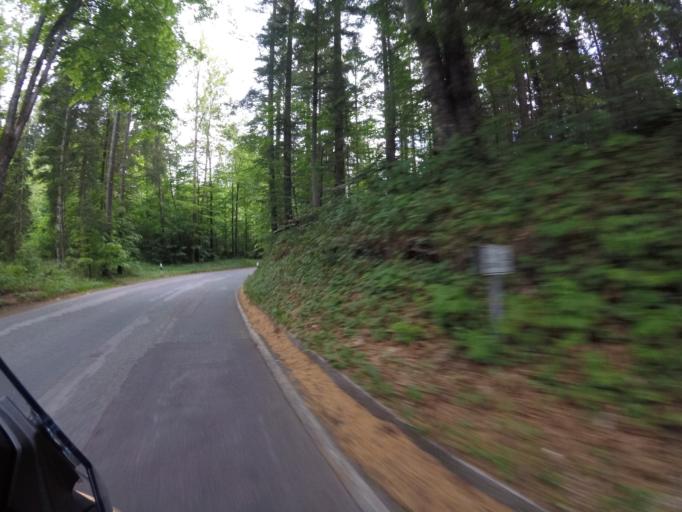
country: DE
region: Bavaria
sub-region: Upper Bavaria
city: Dietramszell
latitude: 47.8123
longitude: 11.5758
